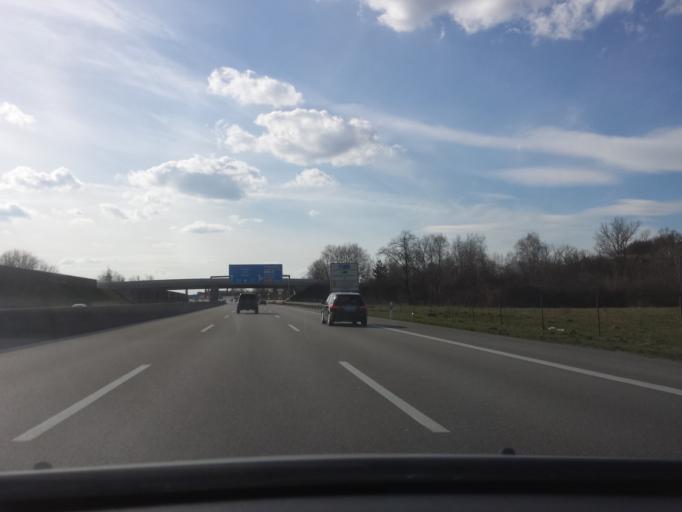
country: DE
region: Bavaria
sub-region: Swabia
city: Gersthofen
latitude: 48.4136
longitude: 10.8975
